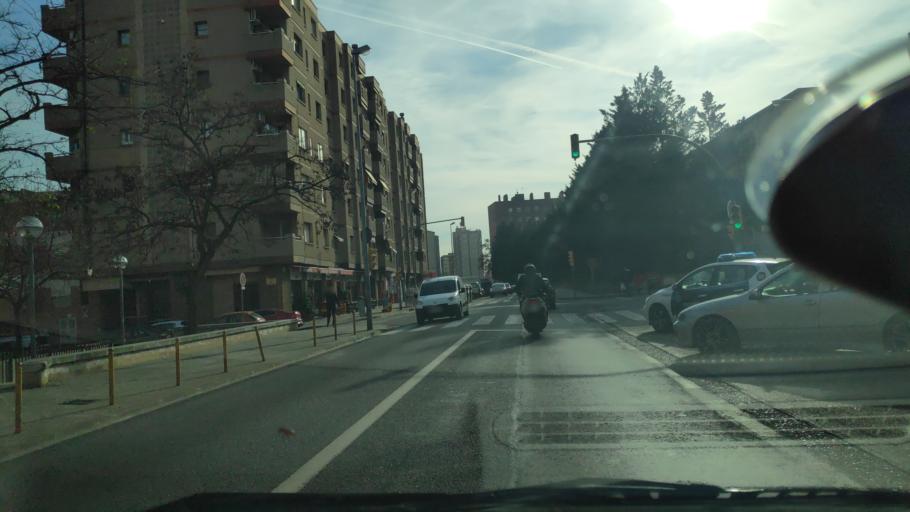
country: ES
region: Catalonia
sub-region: Provincia de Barcelona
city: Sabadell
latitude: 41.5639
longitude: 2.1010
